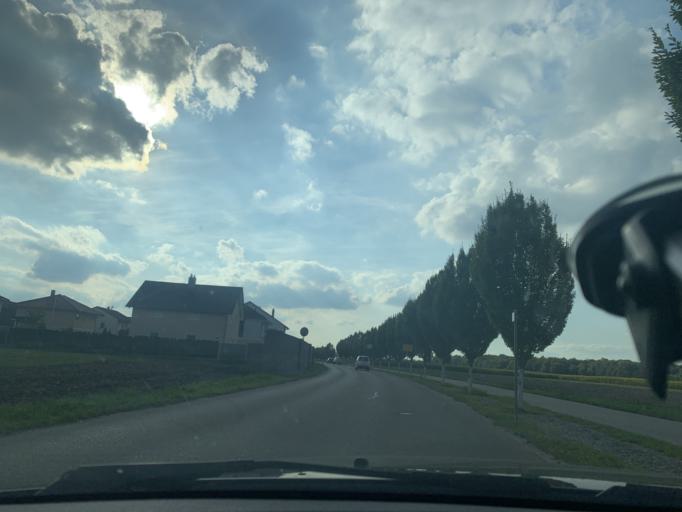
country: DE
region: Bavaria
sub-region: Swabia
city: Kissing
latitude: 48.3107
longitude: 10.9755
